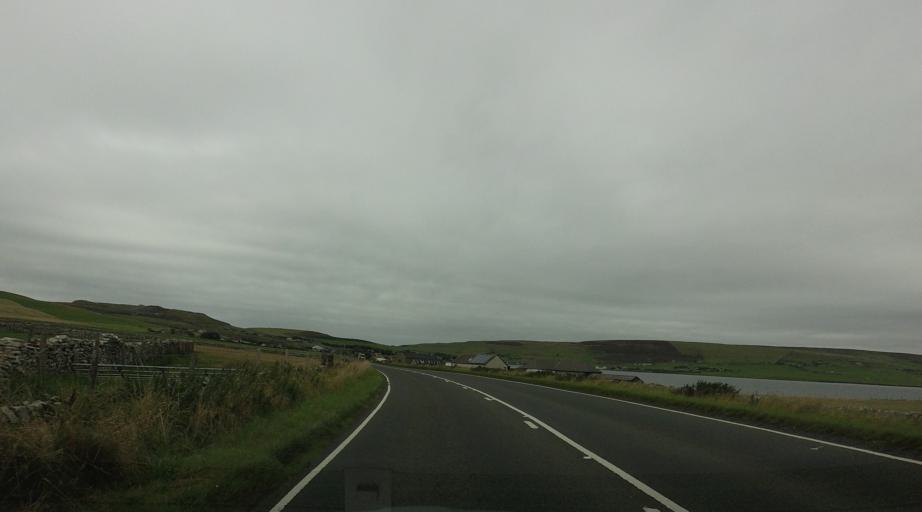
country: GB
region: Scotland
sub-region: Orkney Islands
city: Orkney
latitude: 59.0004
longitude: -3.0922
